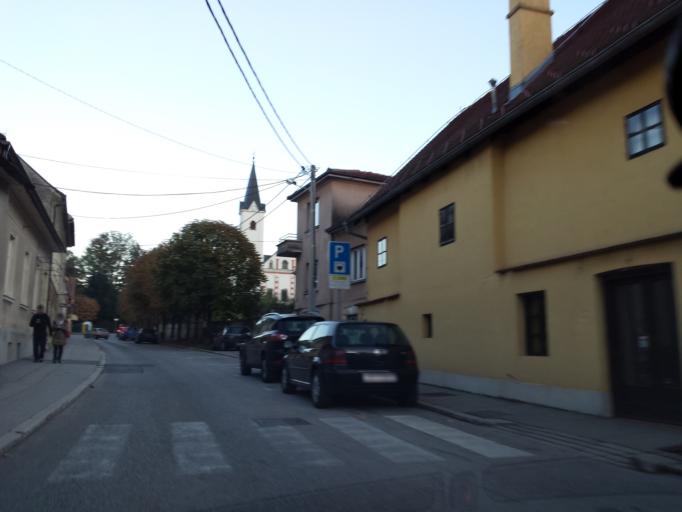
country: HR
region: Zagrebacka
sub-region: Grad Samobor
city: Samobor
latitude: 45.8008
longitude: 15.7117
